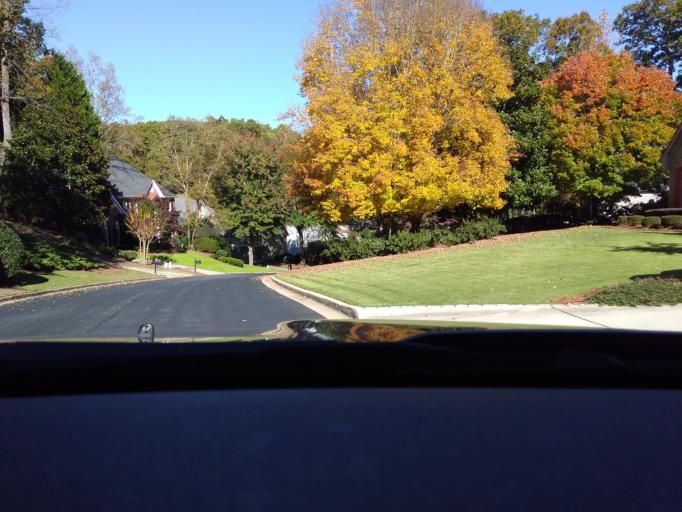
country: US
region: Georgia
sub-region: Fulton County
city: Johns Creek
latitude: 34.0207
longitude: -84.1875
